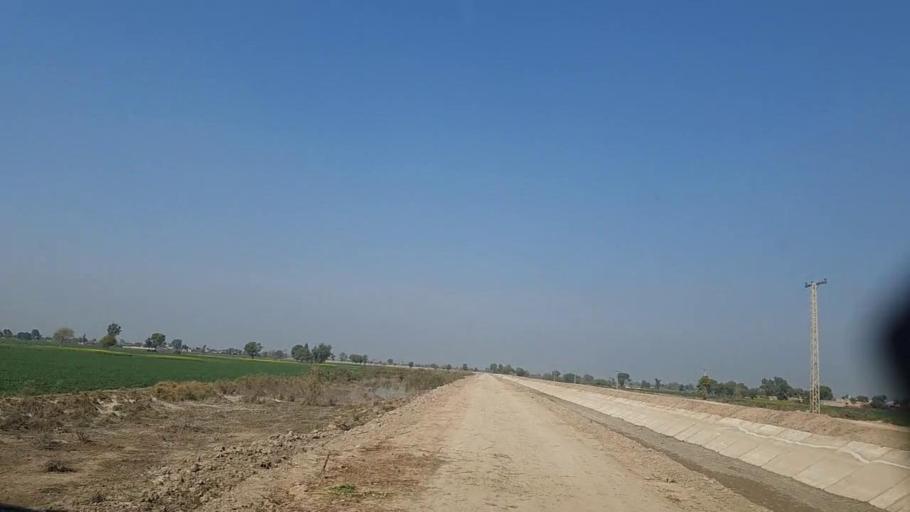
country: PK
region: Sindh
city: Sakrand
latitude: 26.1578
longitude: 68.3277
